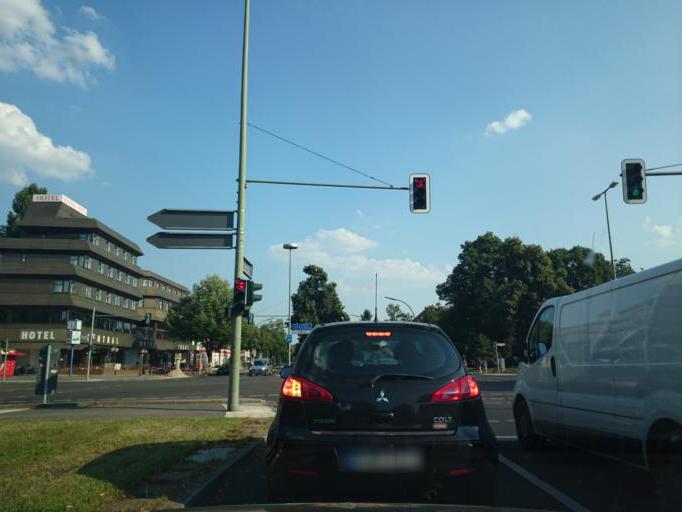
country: DE
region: Berlin
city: Tegel
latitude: 52.5765
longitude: 13.2945
